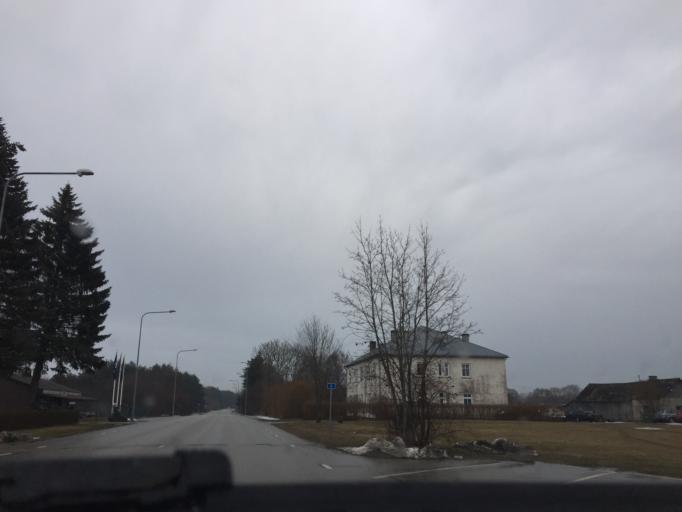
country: EE
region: Saare
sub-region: Orissaare vald
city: Orissaare
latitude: 58.5584
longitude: 23.0858
